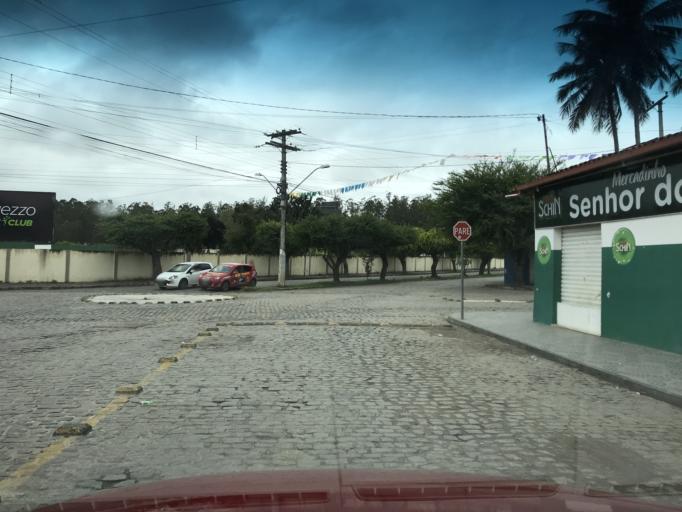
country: BR
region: Bahia
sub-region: Cruz Das Almas
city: Cruz das Almas
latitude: -12.6614
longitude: -39.1014
